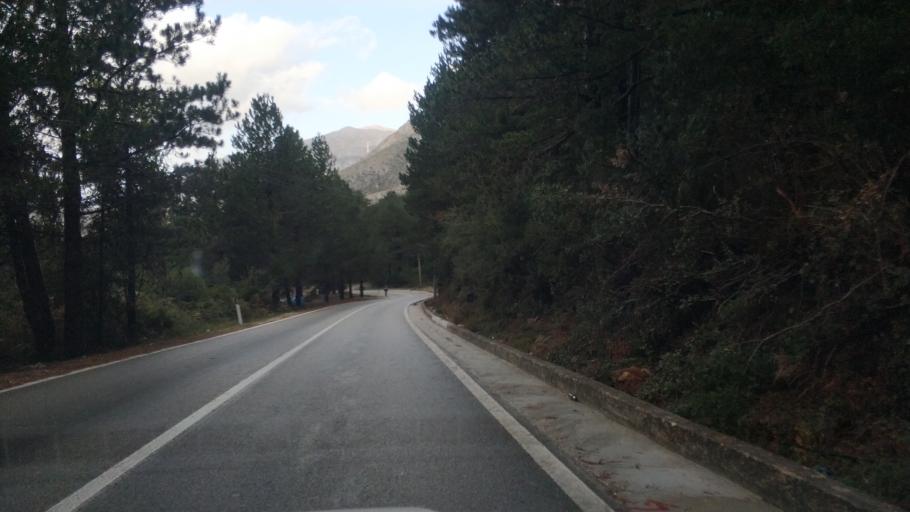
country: AL
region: Vlore
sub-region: Rrethi i Vlores
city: Brataj
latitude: 40.2234
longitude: 19.5785
